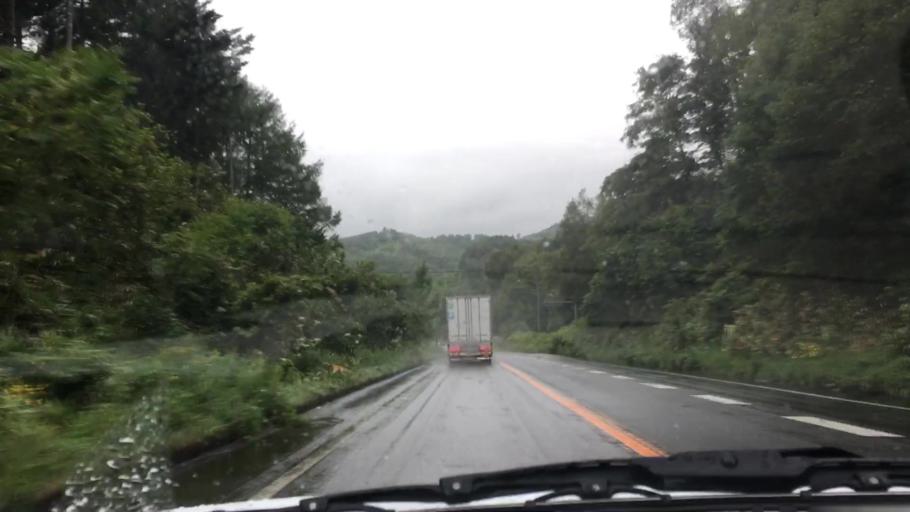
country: JP
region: Hokkaido
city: Niseko Town
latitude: 42.5995
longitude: 140.6642
